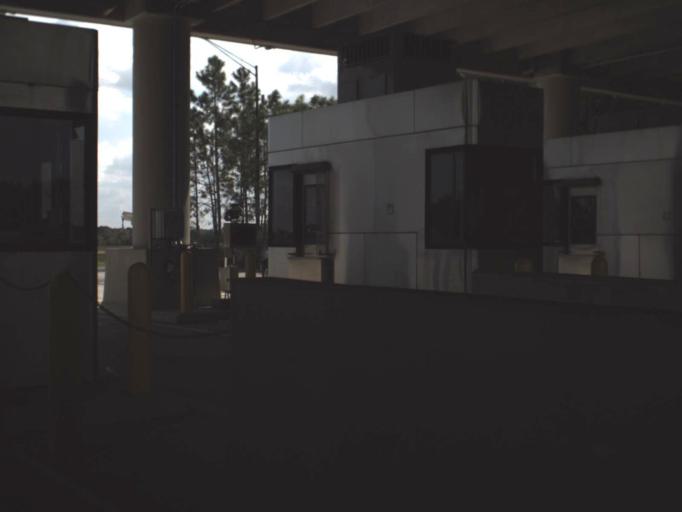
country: US
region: Florida
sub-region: Polk County
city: Lakeland Highlands
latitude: 27.9955
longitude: -81.9346
